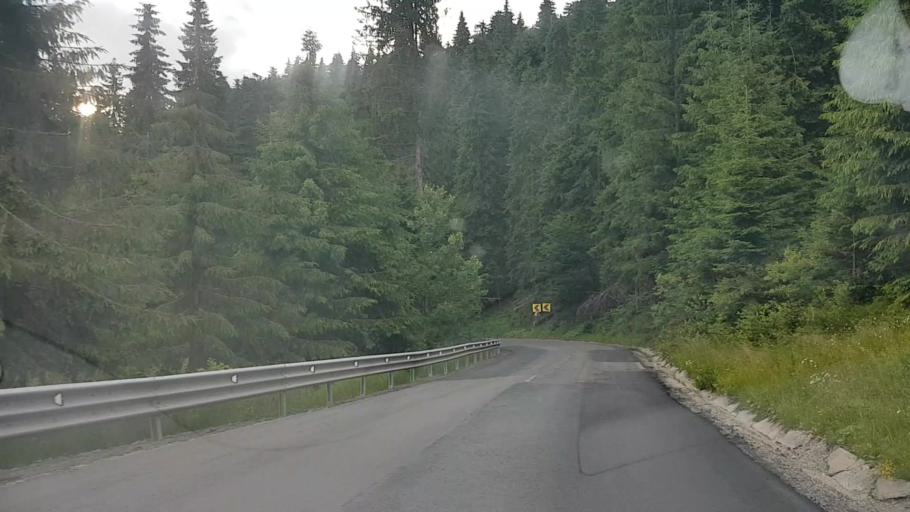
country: RO
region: Harghita
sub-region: Comuna Varsag
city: Varsag
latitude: 46.6423
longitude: 25.2823
